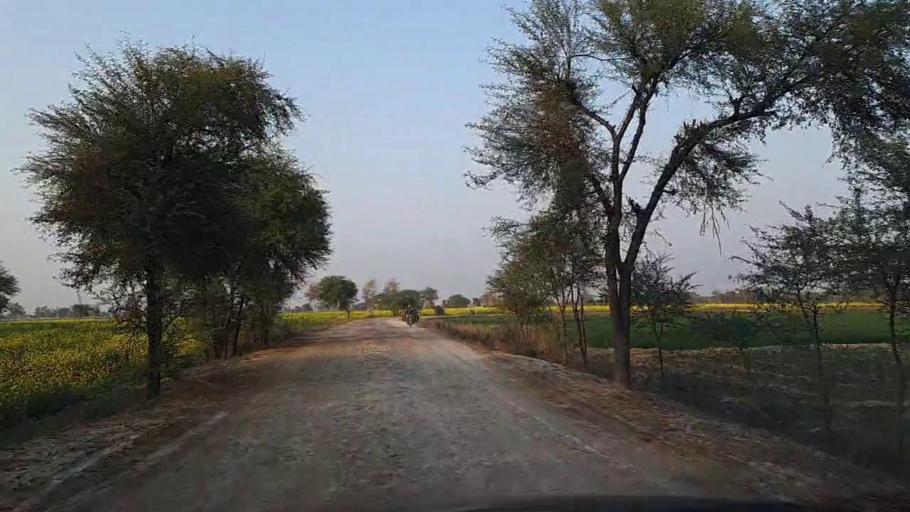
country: PK
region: Sindh
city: Daur
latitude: 26.4302
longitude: 68.3860
